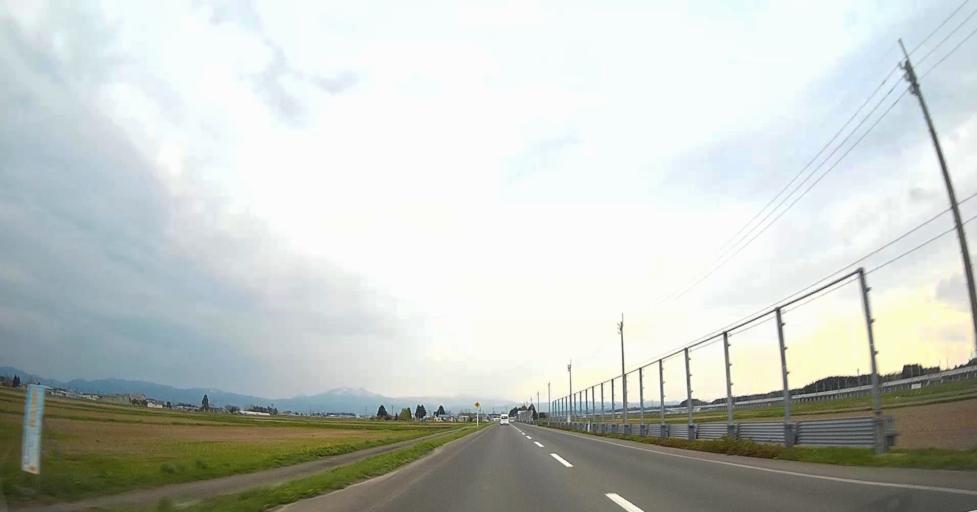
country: JP
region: Aomori
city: Aomori Shi
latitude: 40.8731
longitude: 140.6740
